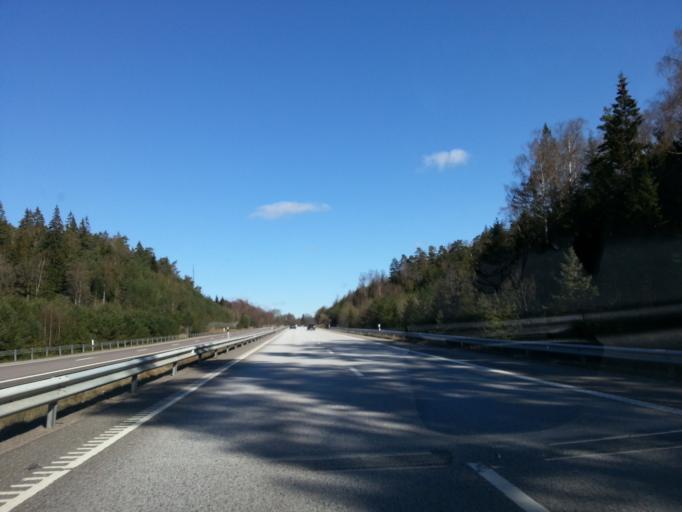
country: SE
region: Vaestra Goetaland
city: Svanesund
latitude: 58.1397
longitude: 11.8853
